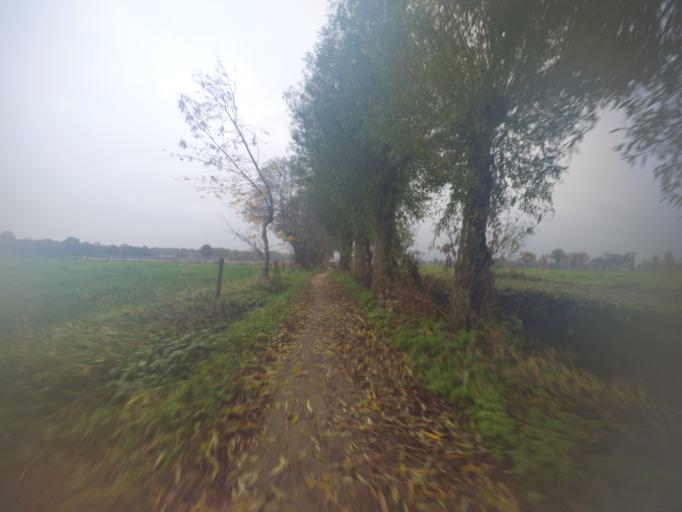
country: NL
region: Gelderland
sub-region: Gemeente Ede
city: Lunteren
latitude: 52.0945
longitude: 5.6044
